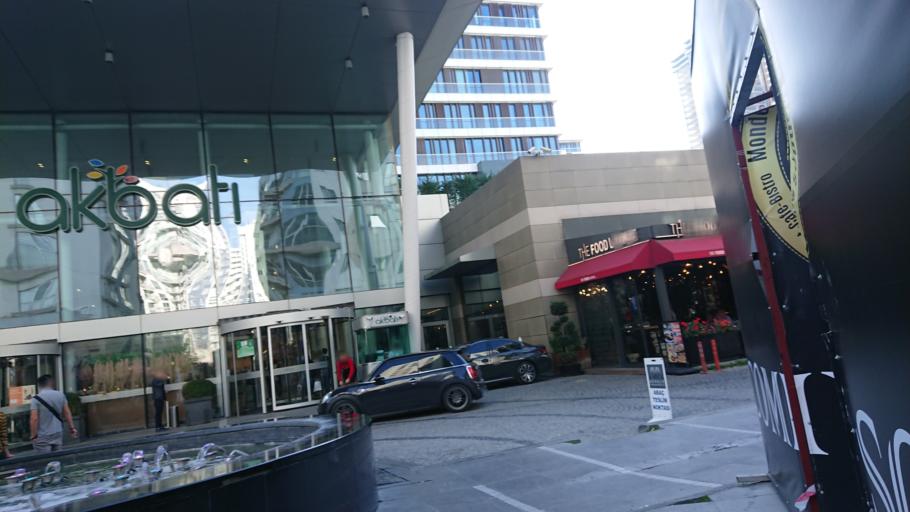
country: TR
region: Istanbul
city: Esenyurt
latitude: 41.0576
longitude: 28.6683
